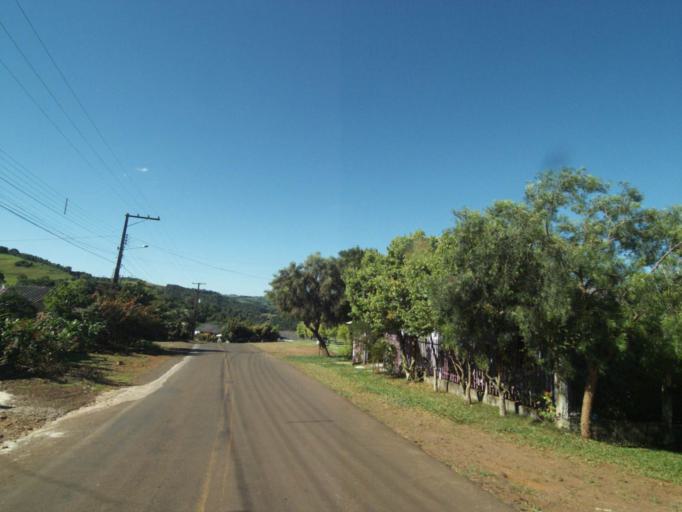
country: BR
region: Parana
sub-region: Ampere
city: Ampere
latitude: -26.1704
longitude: -53.3667
